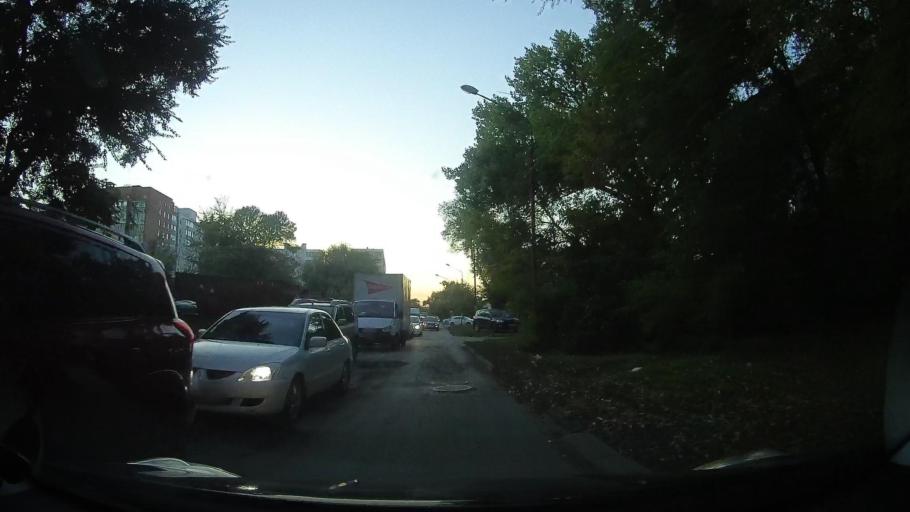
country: RU
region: Rostov
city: Rostov-na-Donu
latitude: 47.2517
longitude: 39.6928
